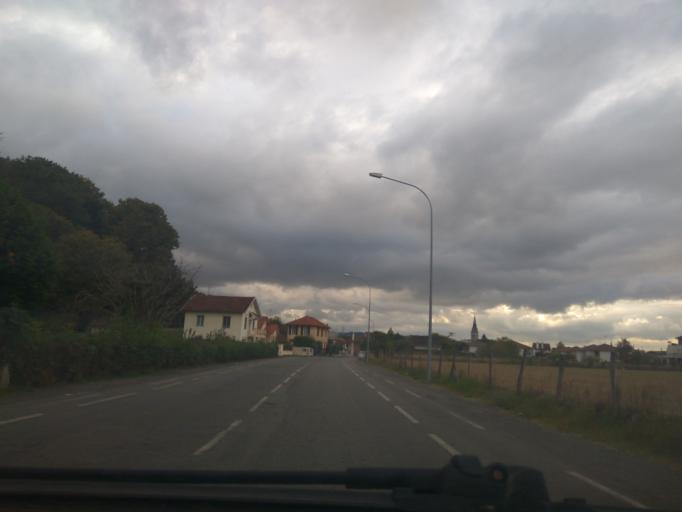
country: FR
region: Aquitaine
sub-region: Departement des Pyrenees-Atlantiques
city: Bizanos
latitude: 43.2877
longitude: -0.3459
